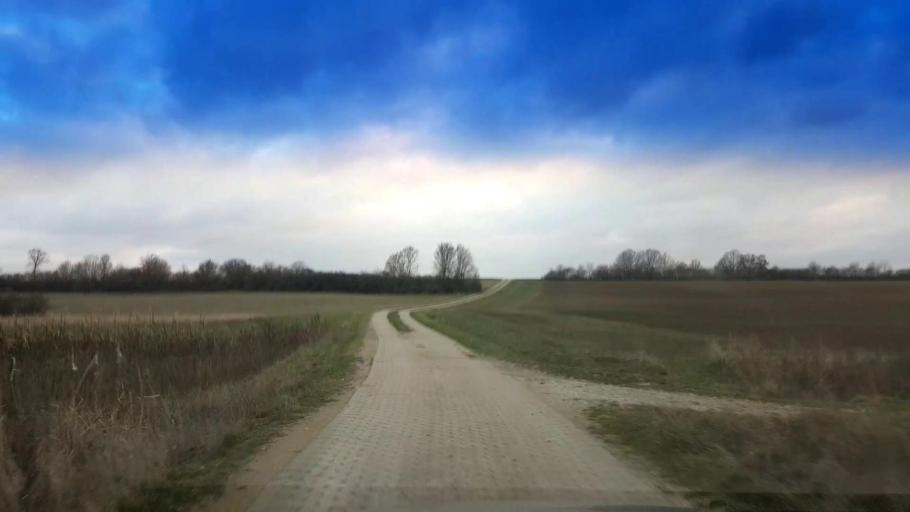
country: DE
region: Bavaria
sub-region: Upper Franconia
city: Schesslitz
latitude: 49.9973
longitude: 11.0395
